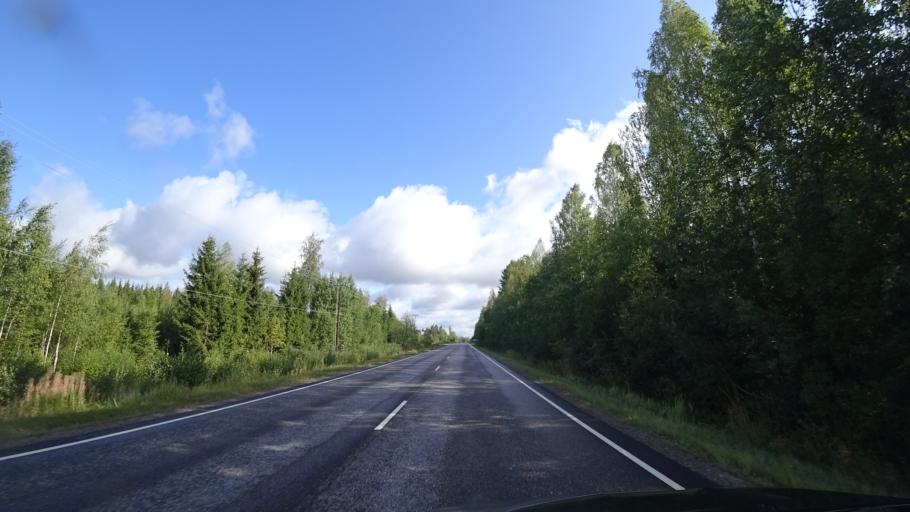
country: FI
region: Uusimaa
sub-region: Helsinki
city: Hyvinge
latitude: 60.5451
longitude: 24.9361
